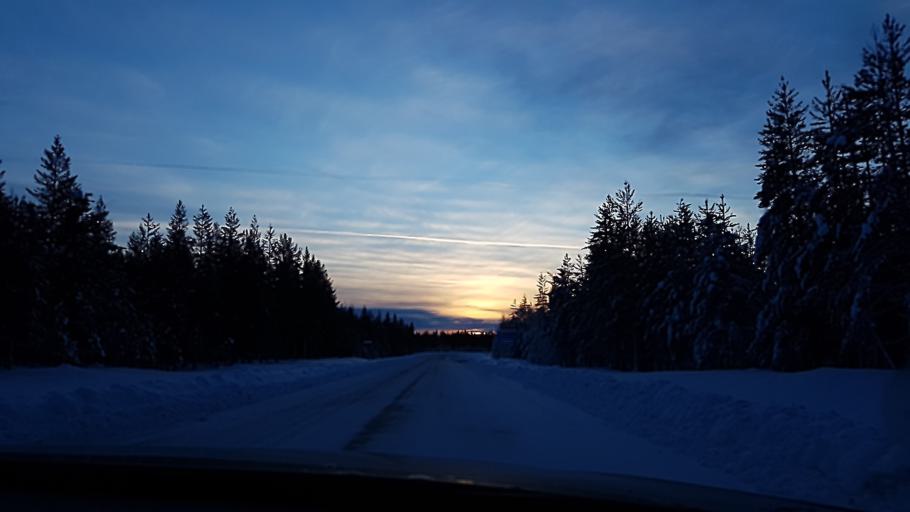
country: SE
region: Norrbotten
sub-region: Jokkmokks Kommun
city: Jokkmokk
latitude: 66.0728
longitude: 20.0753
